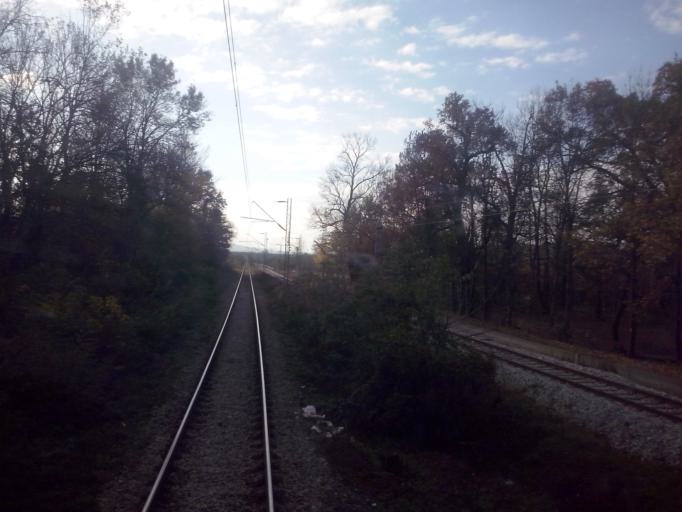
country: RS
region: Central Serbia
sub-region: Belgrade
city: Lazarevac
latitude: 44.4401
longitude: 20.2785
